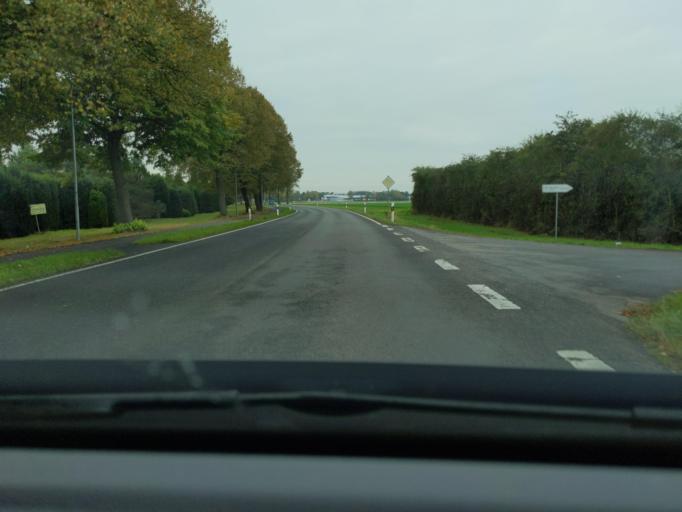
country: DE
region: North Rhine-Westphalia
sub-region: Regierungsbezirk Dusseldorf
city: Kaarst
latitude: 51.2107
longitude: 6.6087
